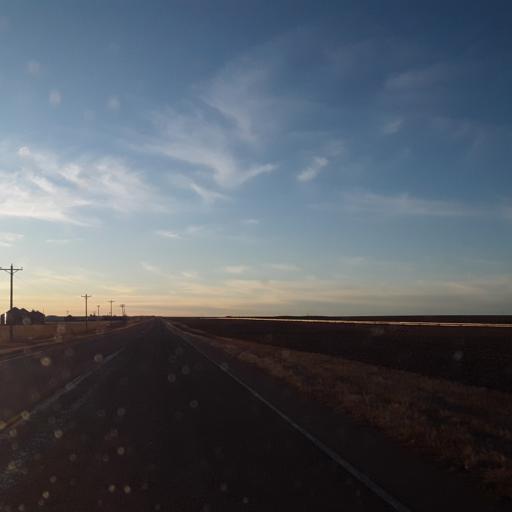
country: US
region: Colorado
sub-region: Cheyenne County
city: Cheyenne Wells
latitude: 38.8143
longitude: -102.3746
